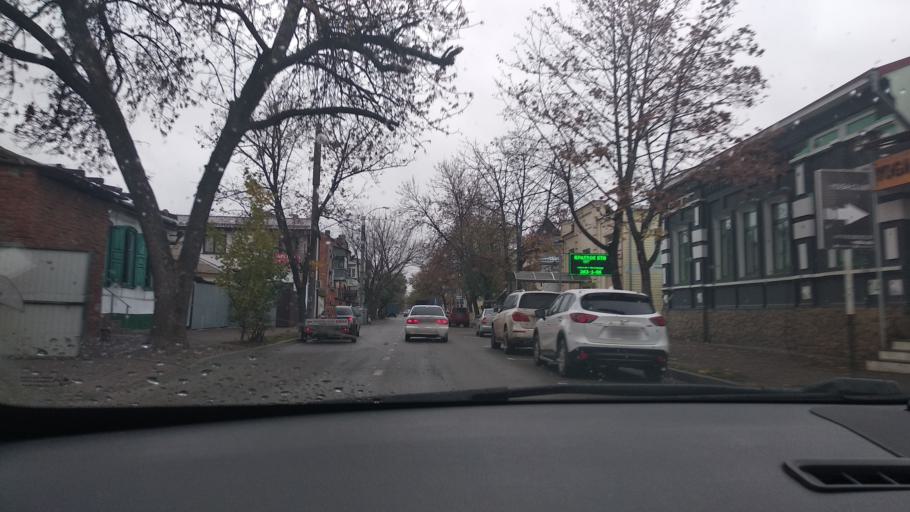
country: RU
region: Krasnodarskiy
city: Krasnodar
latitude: 45.0239
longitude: 38.9812
